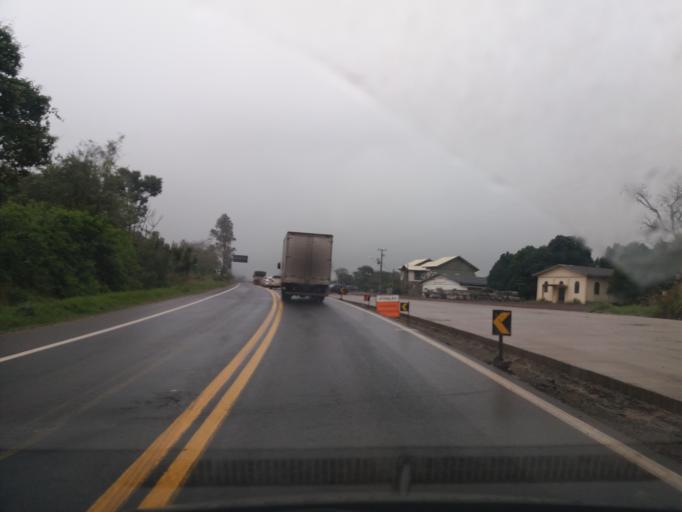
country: BR
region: Parana
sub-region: Realeza
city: Realeza
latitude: -25.4673
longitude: -53.5813
